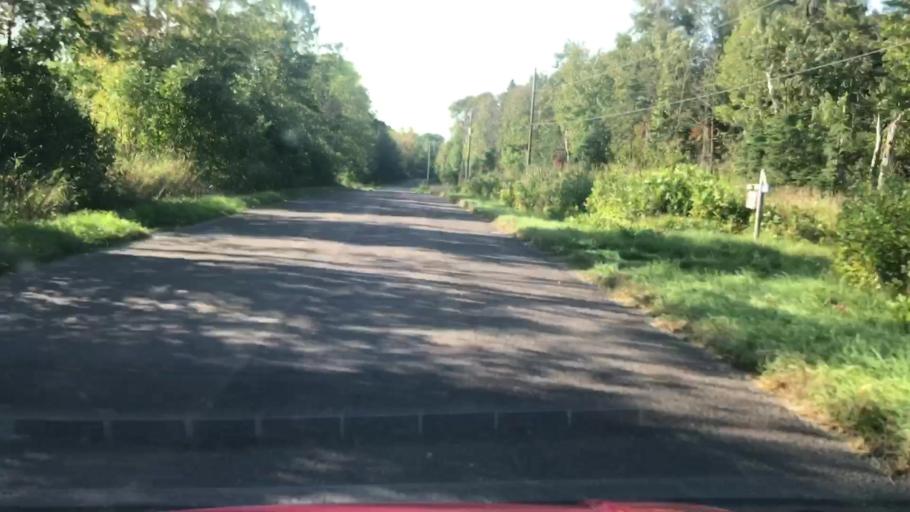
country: US
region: Michigan
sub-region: Chippewa County
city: Sault Ste. Marie
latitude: 46.2941
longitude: -84.0718
